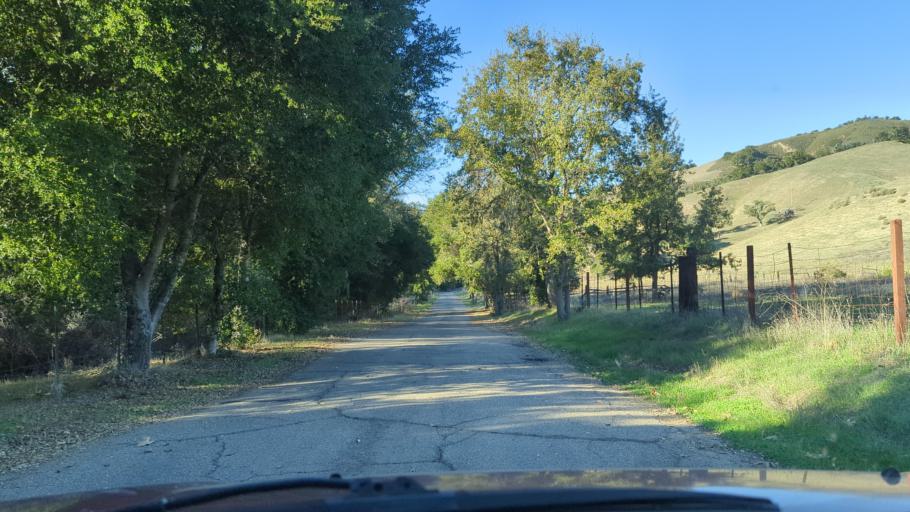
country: US
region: California
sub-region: Santa Barbara County
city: Santa Ynez
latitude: 34.5556
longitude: -120.0822
